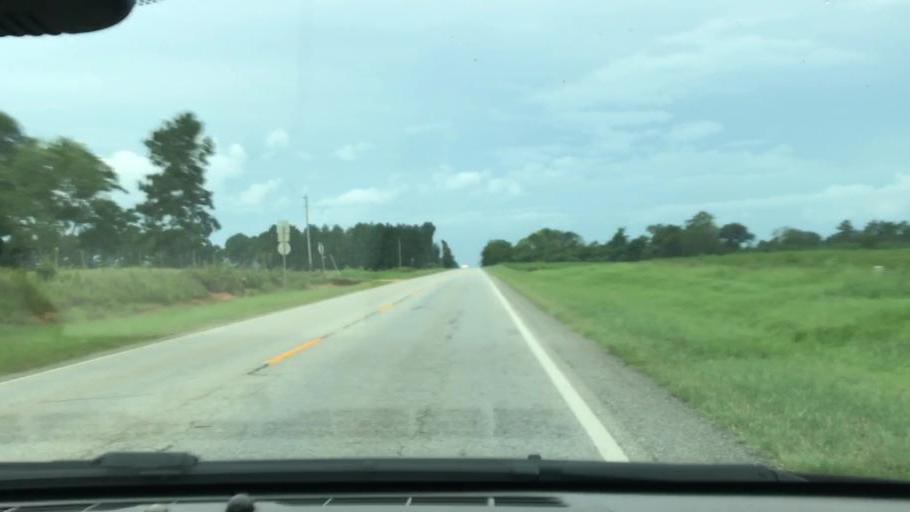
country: US
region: Georgia
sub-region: Early County
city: Blakely
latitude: 31.3287
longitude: -85.0059
